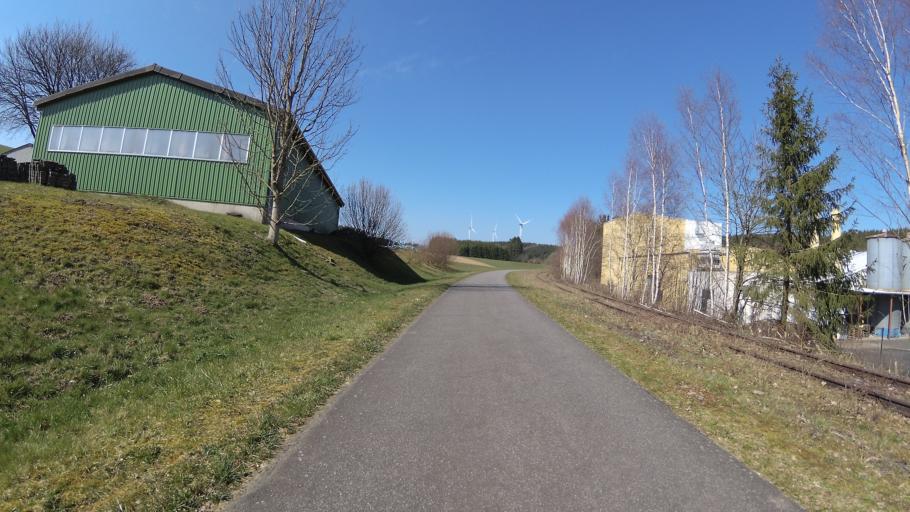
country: DE
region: Rheinland-Pfalz
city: Hermeskeil
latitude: 49.6644
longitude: 6.9301
